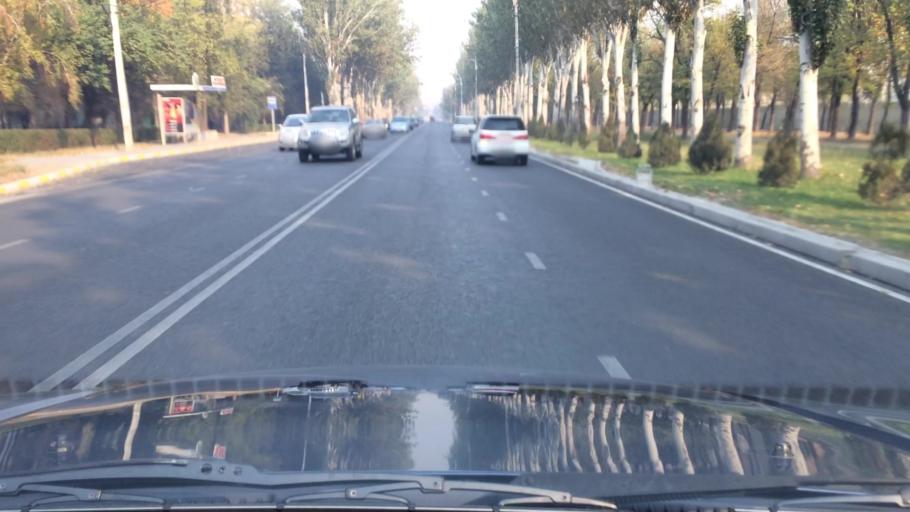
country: KG
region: Chuy
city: Bishkek
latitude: 42.8370
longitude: 74.5857
